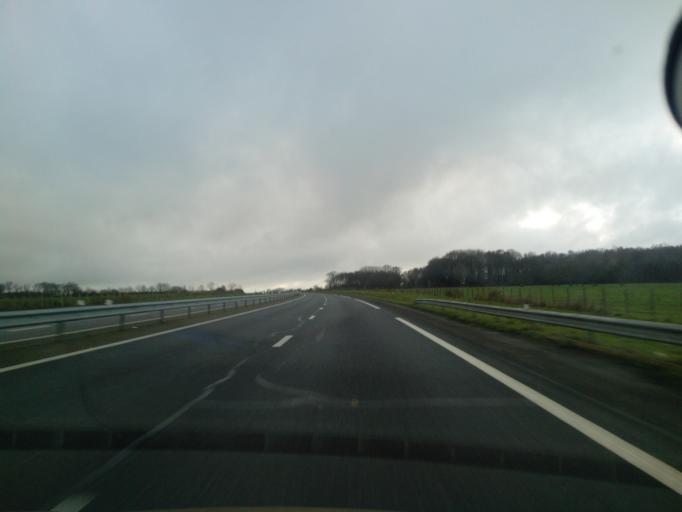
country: FR
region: Brittany
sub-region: Departement des Cotes-d'Armor
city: Plumaugat
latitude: 48.1919
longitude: -2.2972
